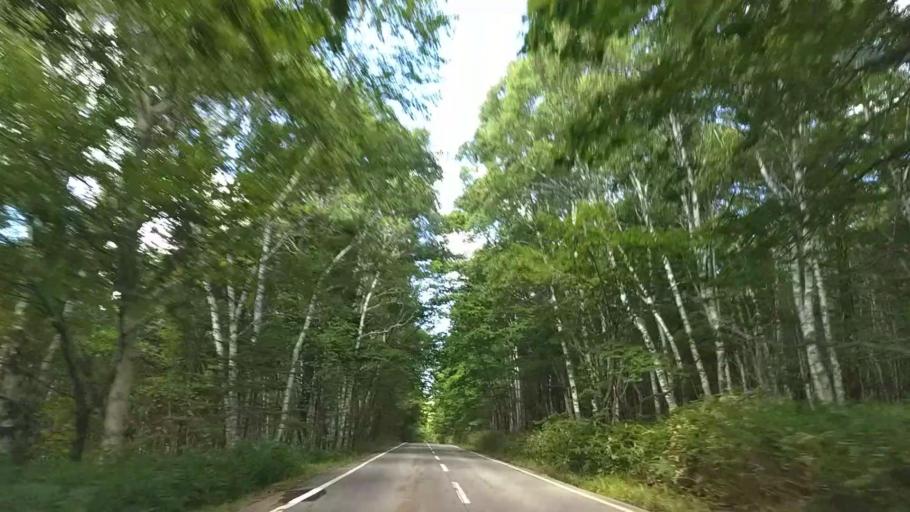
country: JP
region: Nagano
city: Chino
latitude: 36.1101
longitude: 138.2718
